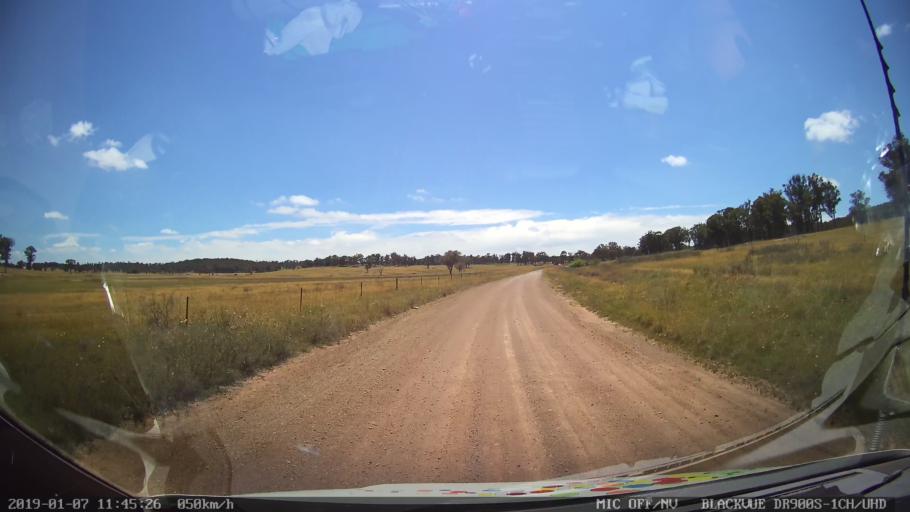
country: AU
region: New South Wales
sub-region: Guyra
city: Guyra
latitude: -30.3460
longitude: 151.6053
